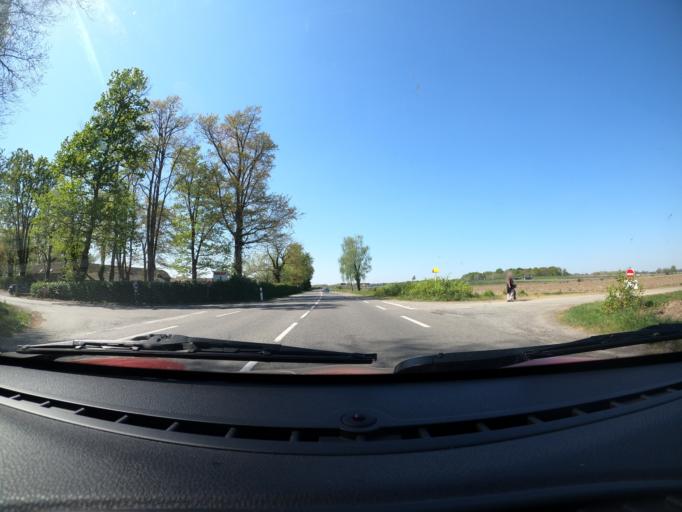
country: FR
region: Aquitaine
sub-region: Departement des Pyrenees-Atlantiques
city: Lescar
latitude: 43.3428
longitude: -0.4126
